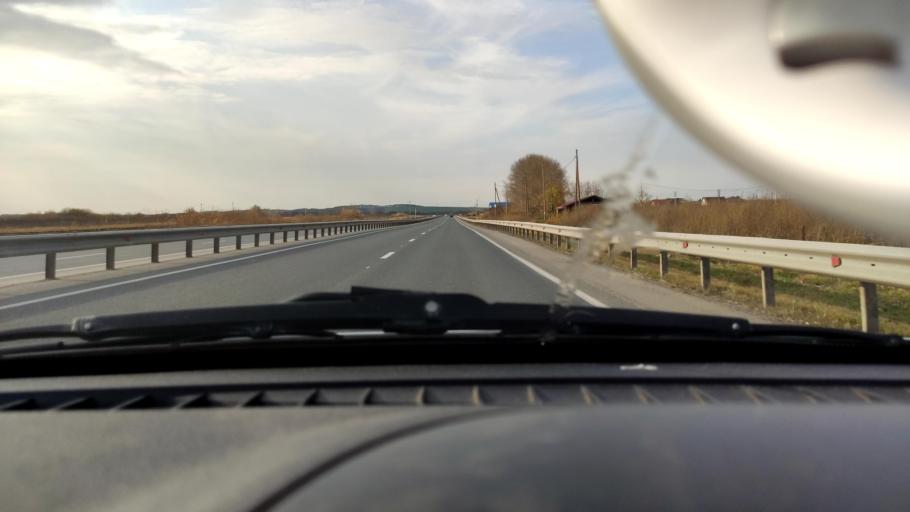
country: RU
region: Perm
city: Kultayevo
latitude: 57.8917
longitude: 55.9526
